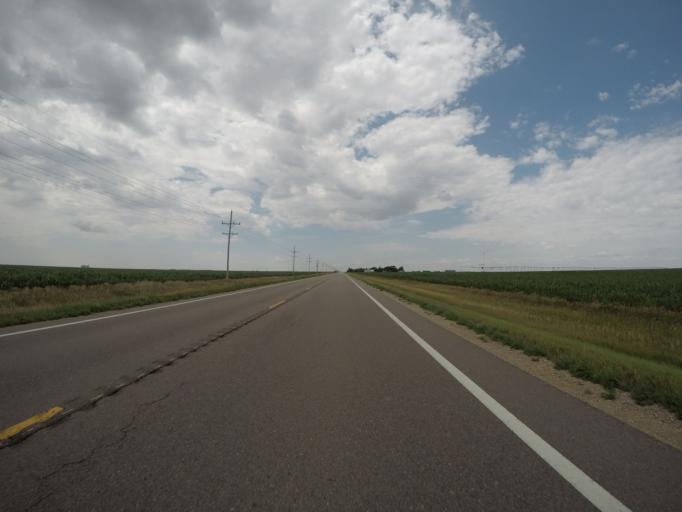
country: US
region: Kansas
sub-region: Thomas County
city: Colby
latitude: 39.3943
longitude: -100.9632
